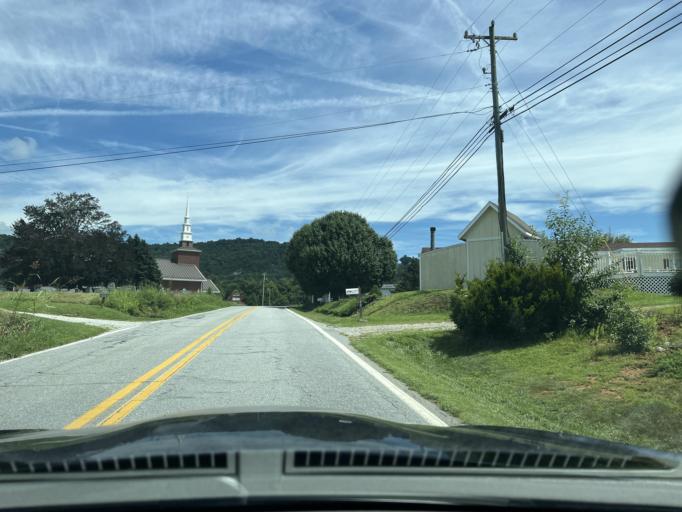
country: US
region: North Carolina
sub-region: Henderson County
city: Edneyville
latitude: 35.3913
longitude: -82.3334
